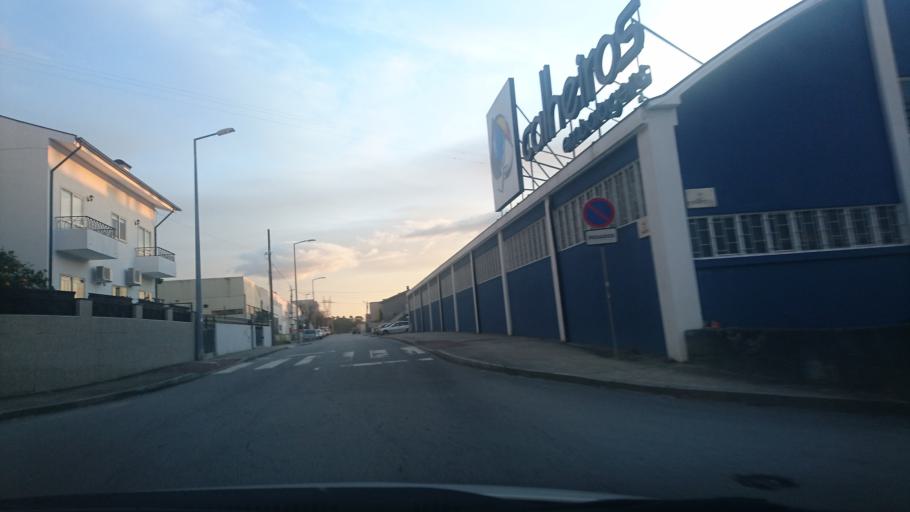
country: PT
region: Porto
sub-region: Gondomar
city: Baguim do Monte
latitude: 41.2040
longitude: -8.5449
